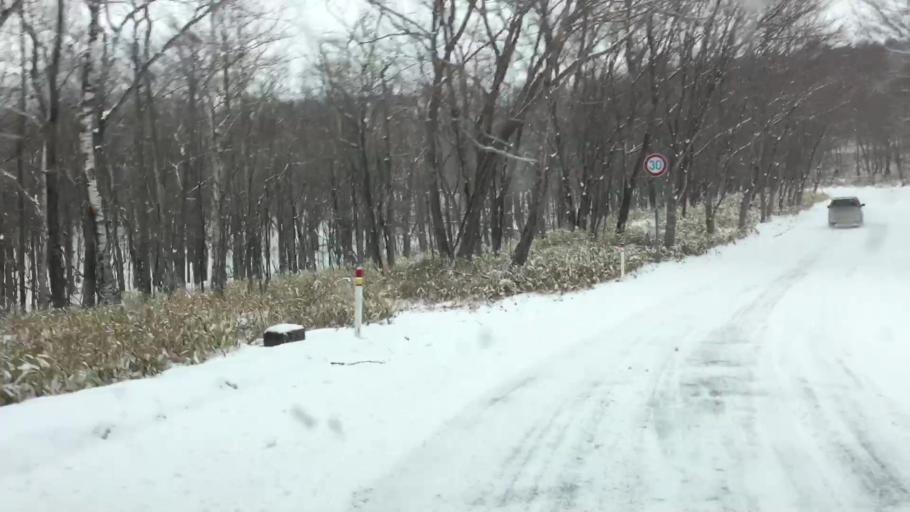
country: JP
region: Tochigi
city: Imaichi
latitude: 36.8881
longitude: 139.7373
